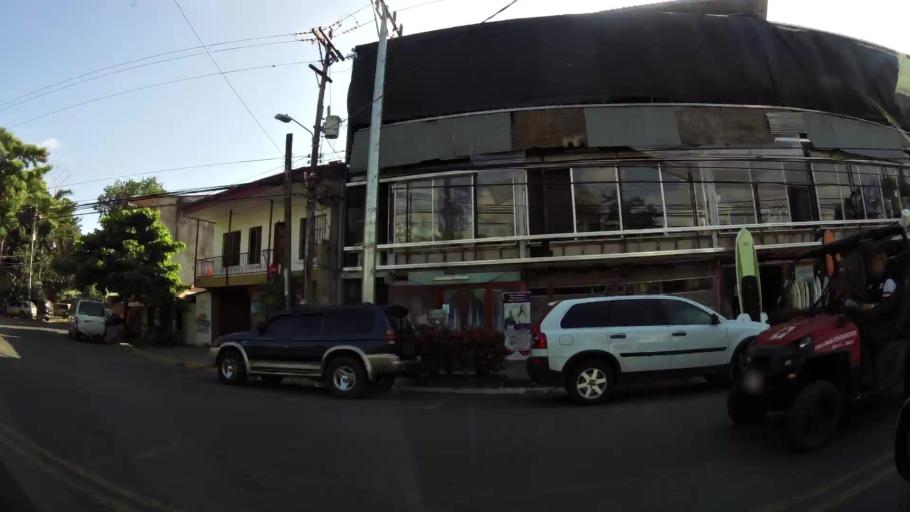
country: CR
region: Puntarenas
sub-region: Canton de Garabito
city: Jaco
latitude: 9.6102
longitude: -84.6243
